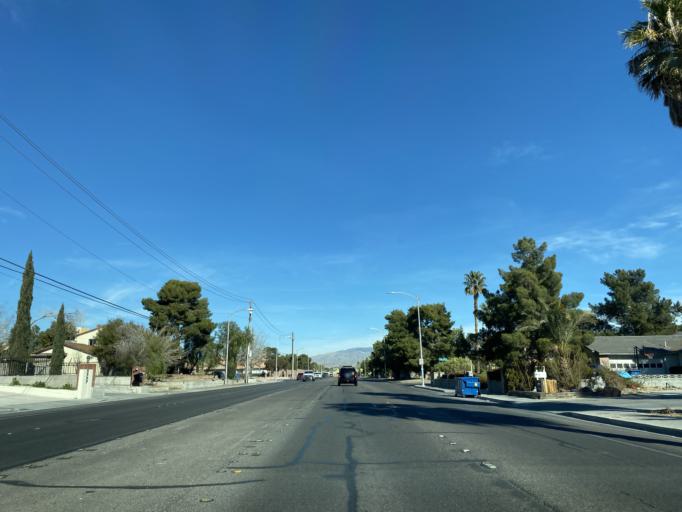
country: US
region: Nevada
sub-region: Clark County
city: Las Vegas
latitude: 36.2123
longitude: -115.2251
